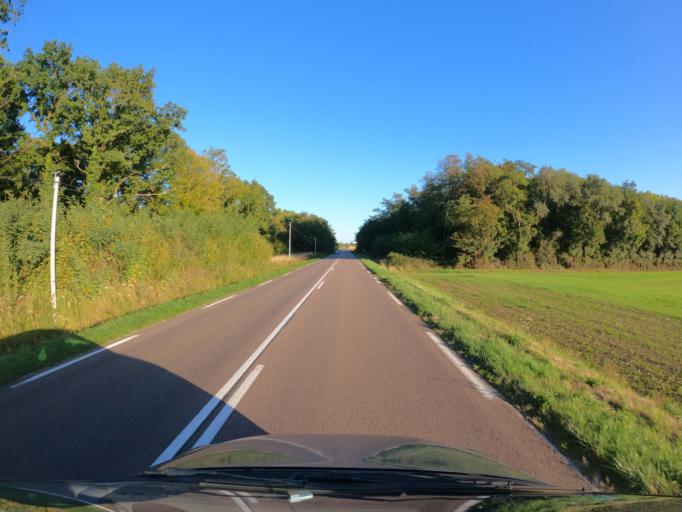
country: FR
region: Bourgogne
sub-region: Departement de Saone-et-Loire
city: Ouroux-sur-Saone
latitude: 46.7658
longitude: 4.9842
